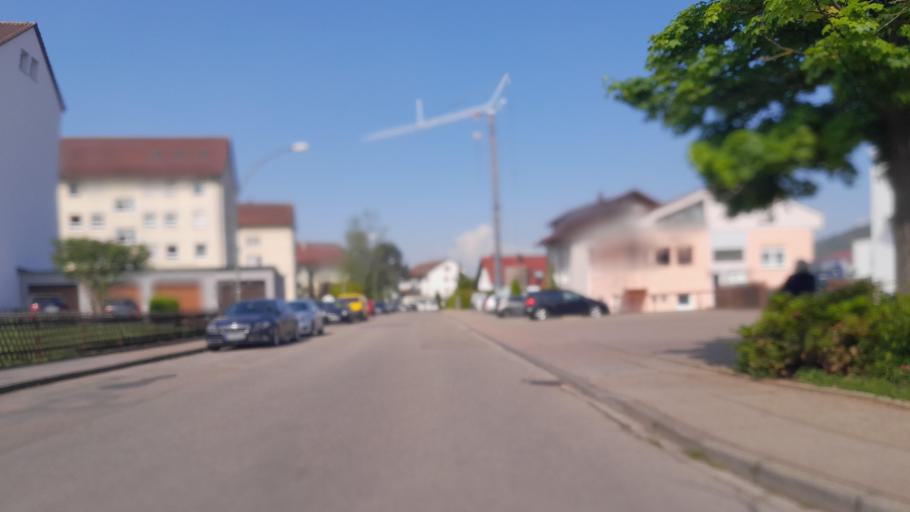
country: DE
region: Baden-Wuerttemberg
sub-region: Regierungsbezirk Stuttgart
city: Donzdorf
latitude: 48.6822
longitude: 9.8043
